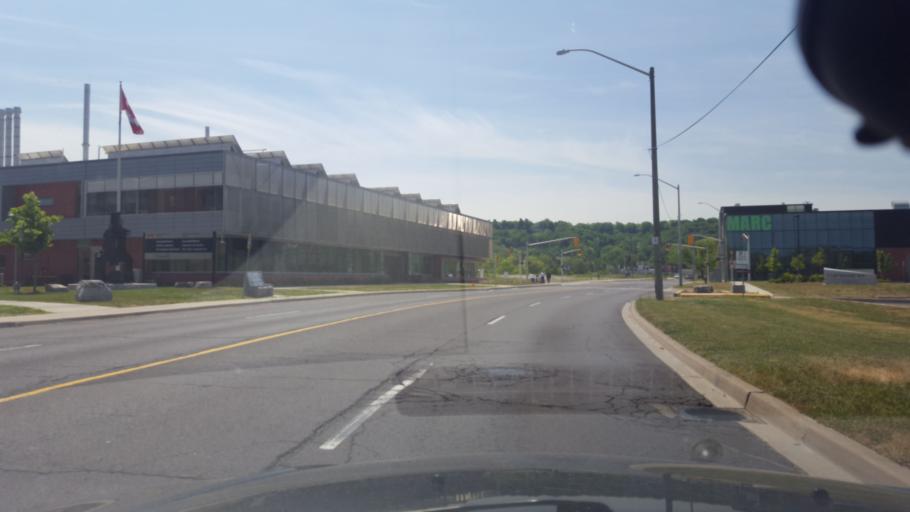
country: CA
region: Ontario
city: Hamilton
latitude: 43.2568
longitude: -79.9014
